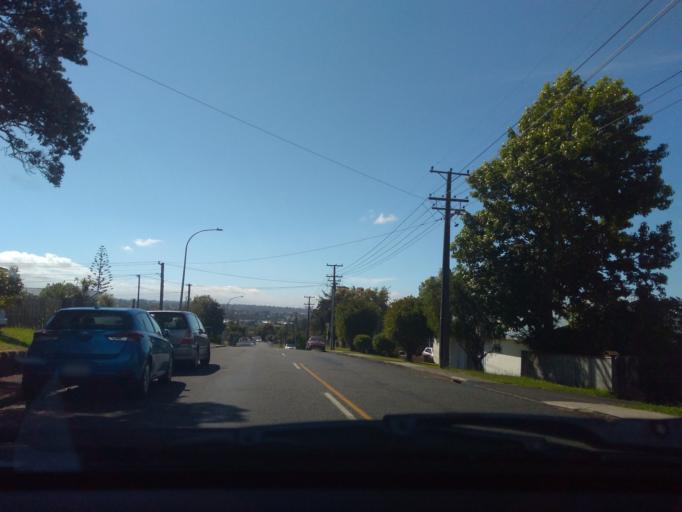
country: NZ
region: Auckland
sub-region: Auckland
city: Waitakere
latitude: -36.8972
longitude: 174.6423
